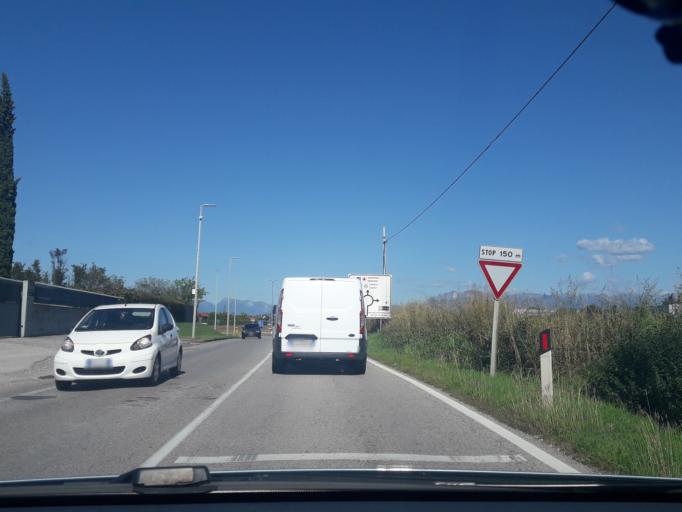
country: IT
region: Friuli Venezia Giulia
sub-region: Provincia di Udine
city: Basaldella
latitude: 46.0280
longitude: 13.2382
